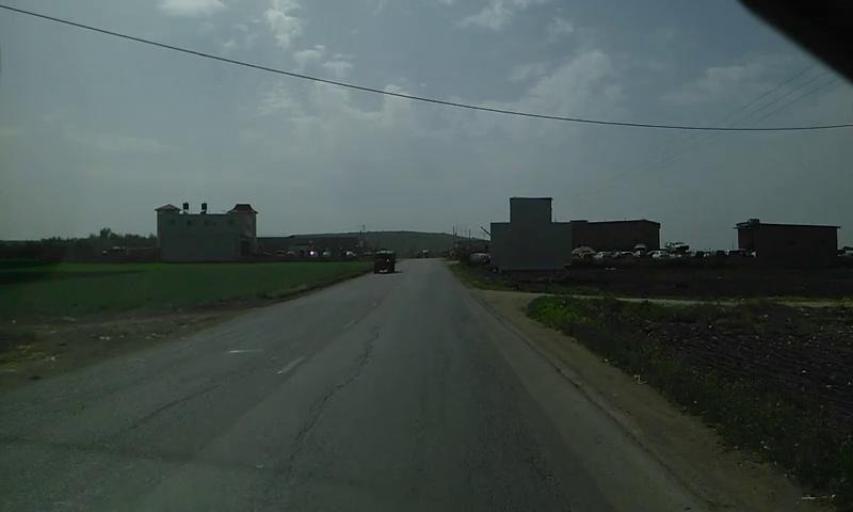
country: PS
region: West Bank
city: Ash Shuhada'
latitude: 32.4262
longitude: 35.2537
